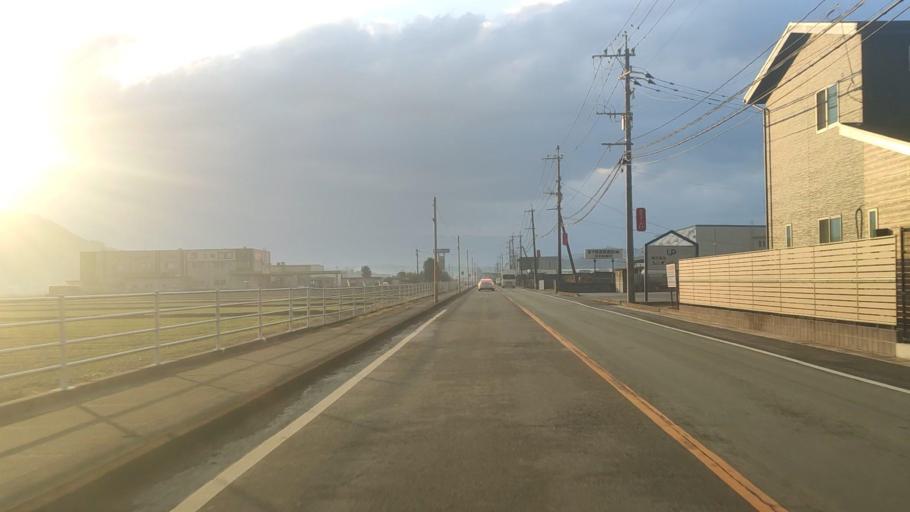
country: JP
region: Kumamoto
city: Uto
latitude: 32.7118
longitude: 130.7747
